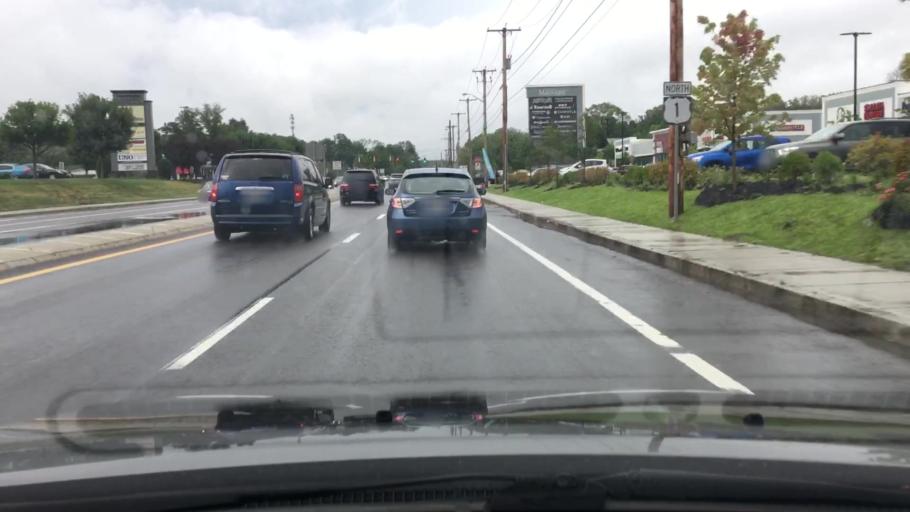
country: US
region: Rhode Island
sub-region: Providence County
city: Valley Falls
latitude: 41.9231
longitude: -71.3571
